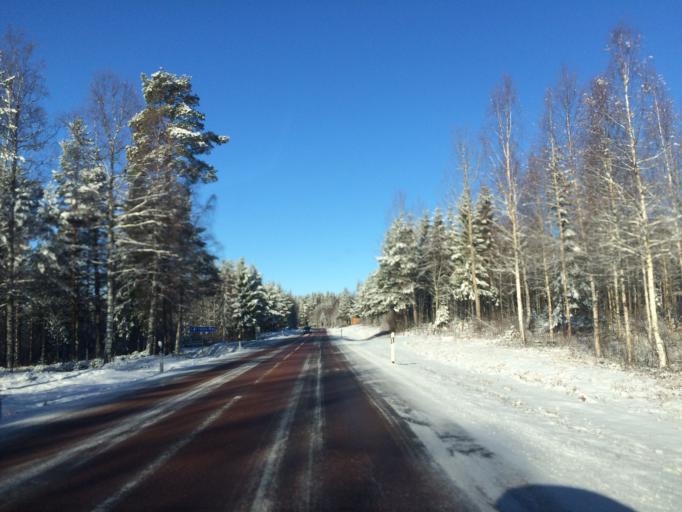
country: SE
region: Dalarna
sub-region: Vansbro Kommun
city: Vansbro
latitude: 60.8463
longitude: 14.1649
